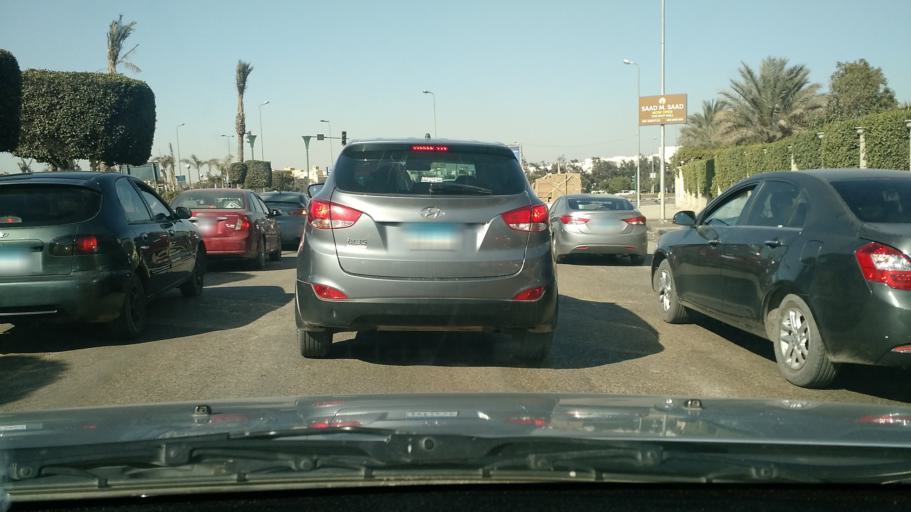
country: EG
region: Muhafazat al Qahirah
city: Cairo
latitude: 29.9987
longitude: 31.4069
